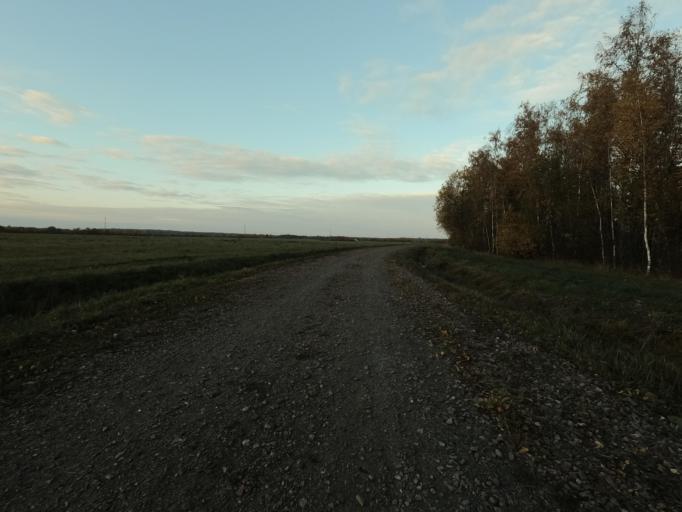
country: RU
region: Leningrad
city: Mga
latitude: 59.7836
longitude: 31.1960
